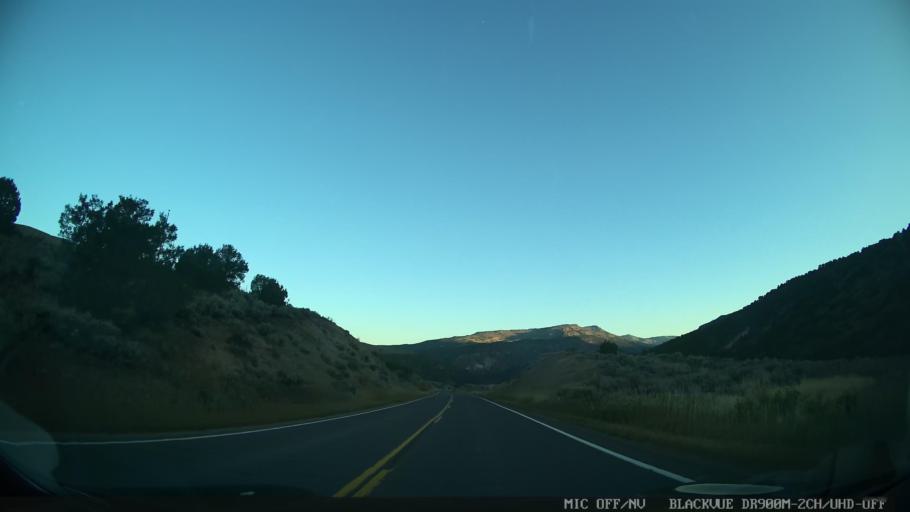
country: US
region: Colorado
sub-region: Eagle County
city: Edwards
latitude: 39.8360
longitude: -106.6390
